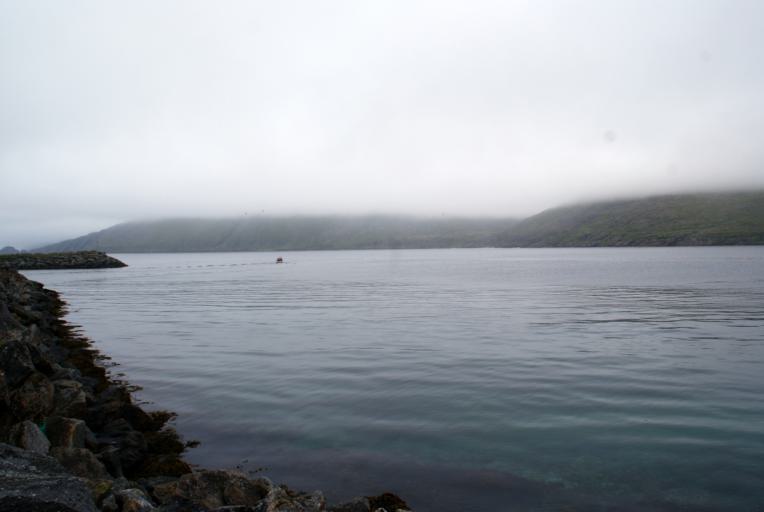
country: NO
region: Finnmark Fylke
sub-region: Nordkapp
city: Honningsvag
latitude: 71.1114
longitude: 25.8302
